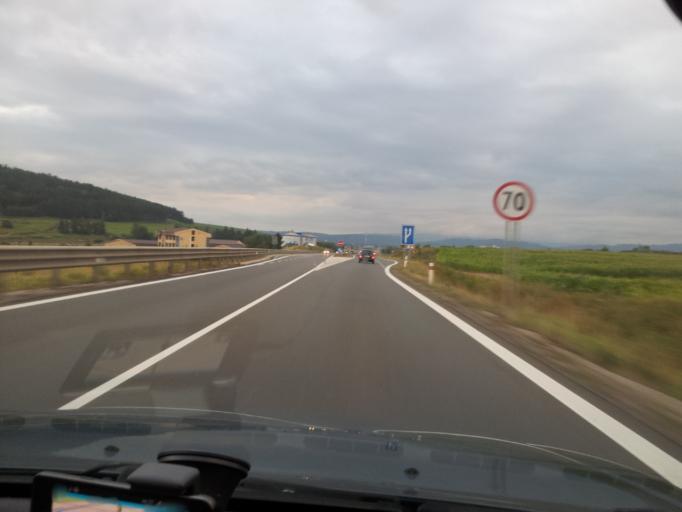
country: SK
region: Presovsky
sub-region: Okres Poprad
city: Poprad
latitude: 49.1000
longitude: 20.3423
